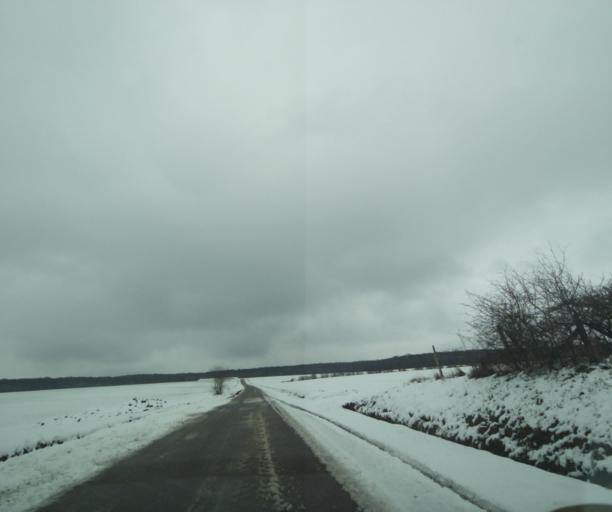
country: FR
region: Champagne-Ardenne
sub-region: Departement de la Haute-Marne
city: Laneuville-a-Remy
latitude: 48.4005
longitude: 4.8574
